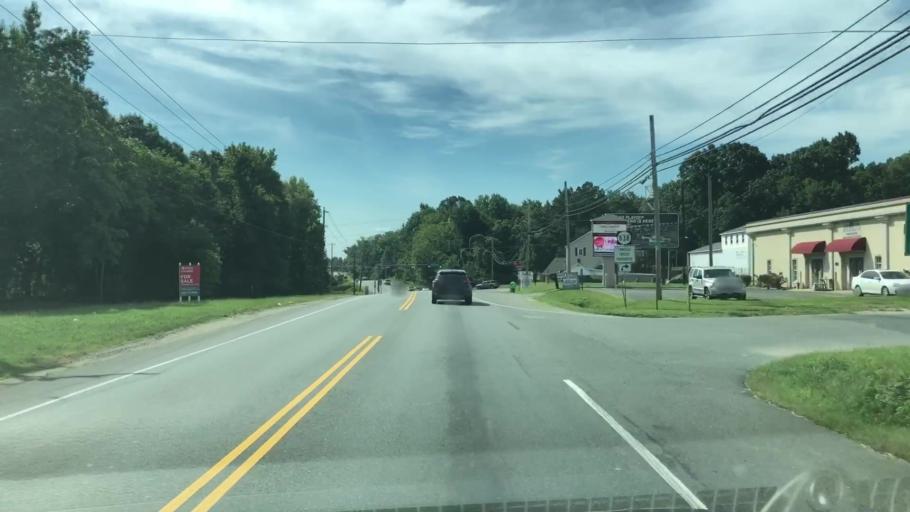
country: US
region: Virginia
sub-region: City of Fredericksburg
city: Fredericksburg
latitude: 38.2776
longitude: -77.4524
